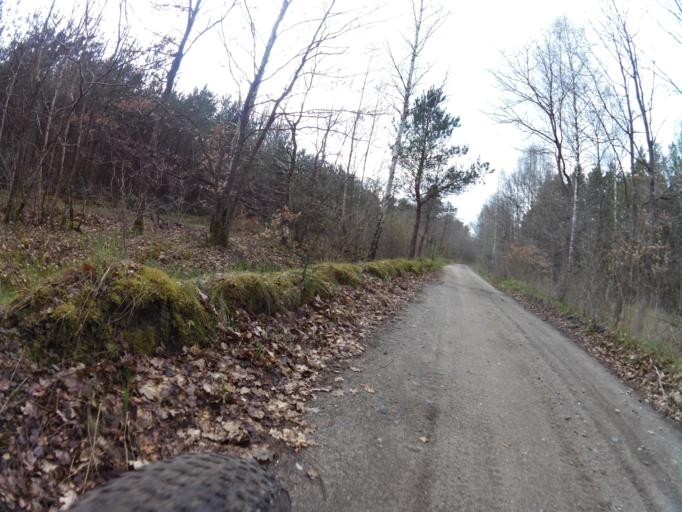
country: PL
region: West Pomeranian Voivodeship
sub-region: Powiat slawienski
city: Slawno
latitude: 54.3214
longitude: 16.7693
